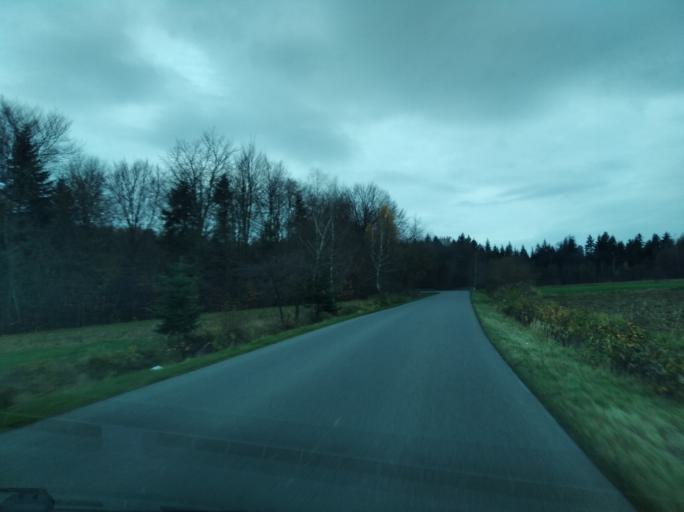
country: PL
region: Subcarpathian Voivodeship
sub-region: Powiat ropczycko-sedziszowski
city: Zagorzyce
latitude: 49.9689
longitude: 21.6984
